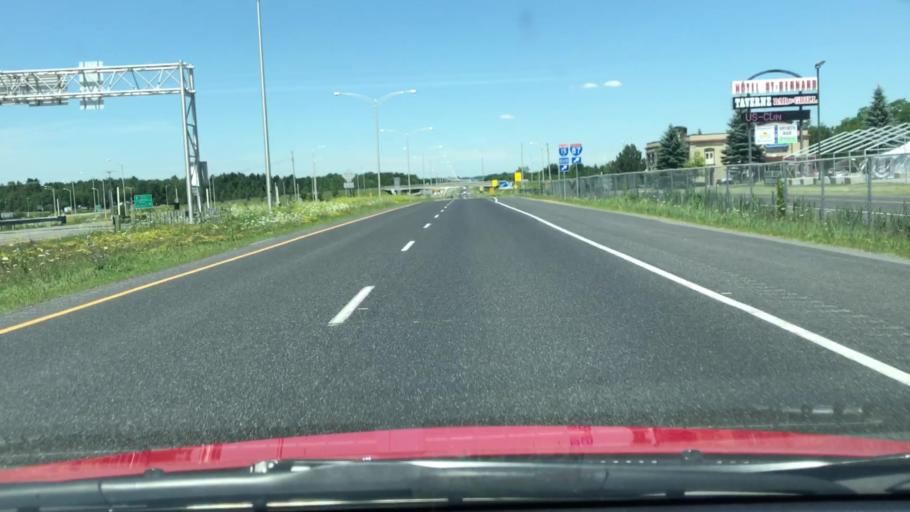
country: US
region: New York
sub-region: Clinton County
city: Champlain
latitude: 45.0160
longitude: -73.4526
